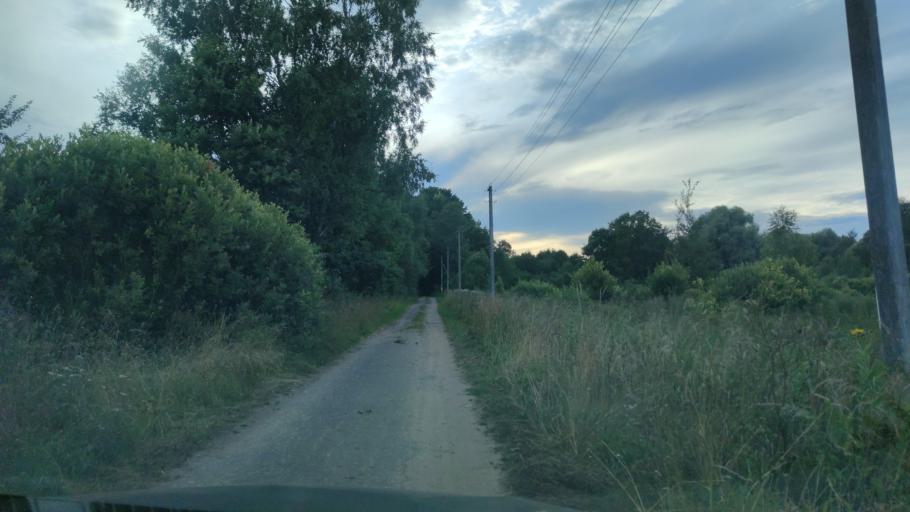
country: BY
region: Vitebsk
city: Mosar
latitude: 55.1231
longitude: 27.1795
